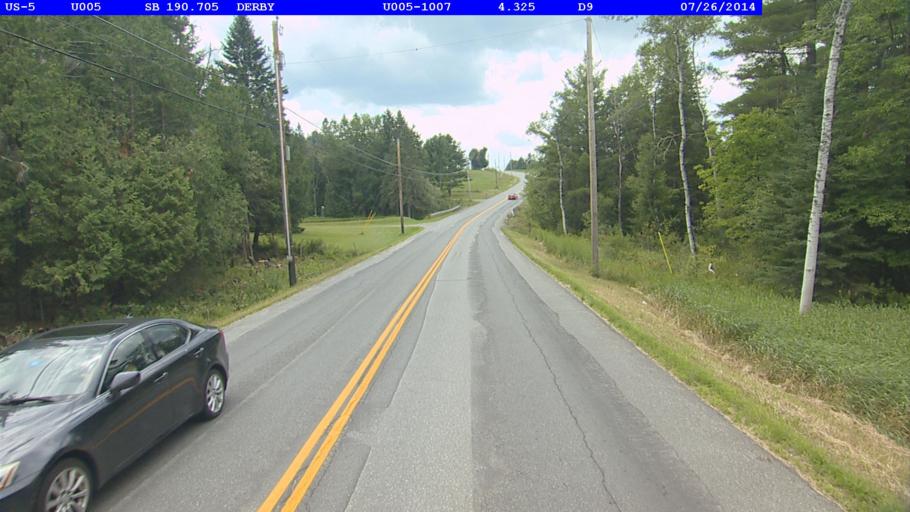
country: US
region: Vermont
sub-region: Orleans County
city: Newport
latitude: 44.9840
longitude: -72.1082
